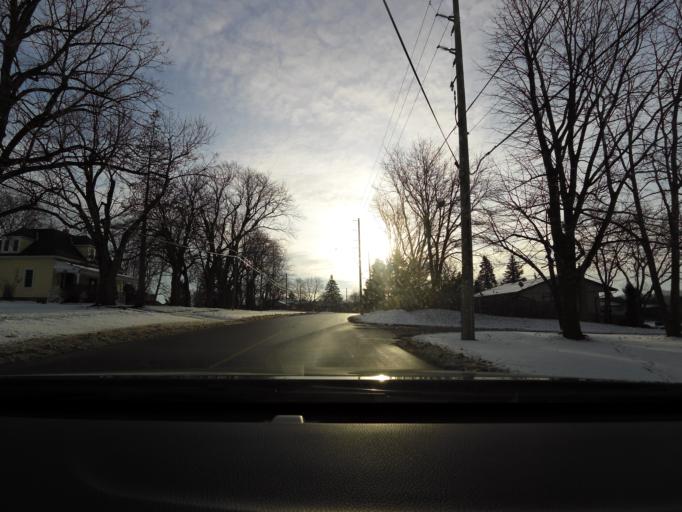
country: CA
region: Ontario
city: Ancaster
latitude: 43.0702
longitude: -79.9415
